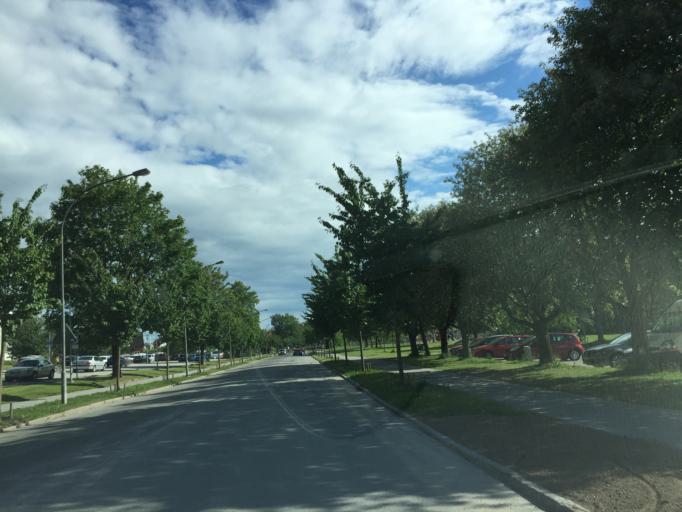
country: SE
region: OErebro
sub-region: Orebro Kommun
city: Orebro
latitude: 59.2882
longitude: 15.2278
